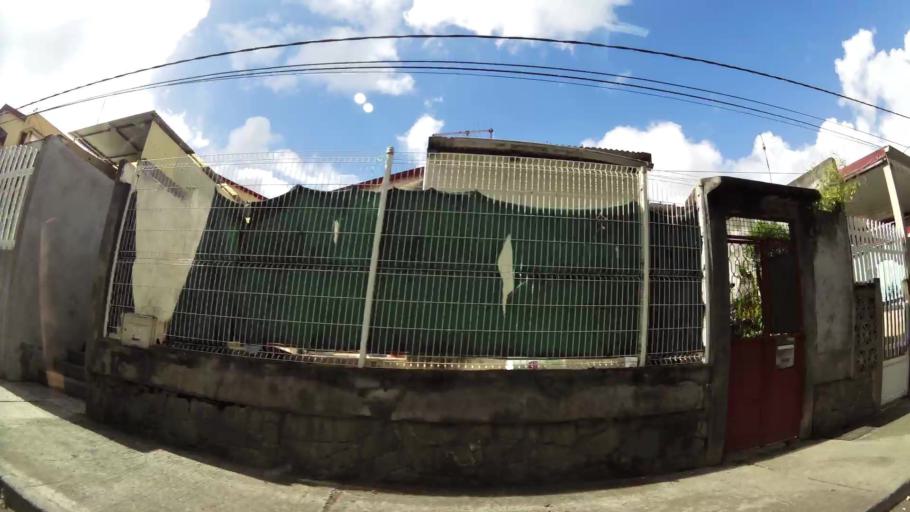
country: MQ
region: Martinique
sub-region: Martinique
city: Fort-de-France
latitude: 14.6050
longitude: -61.0565
